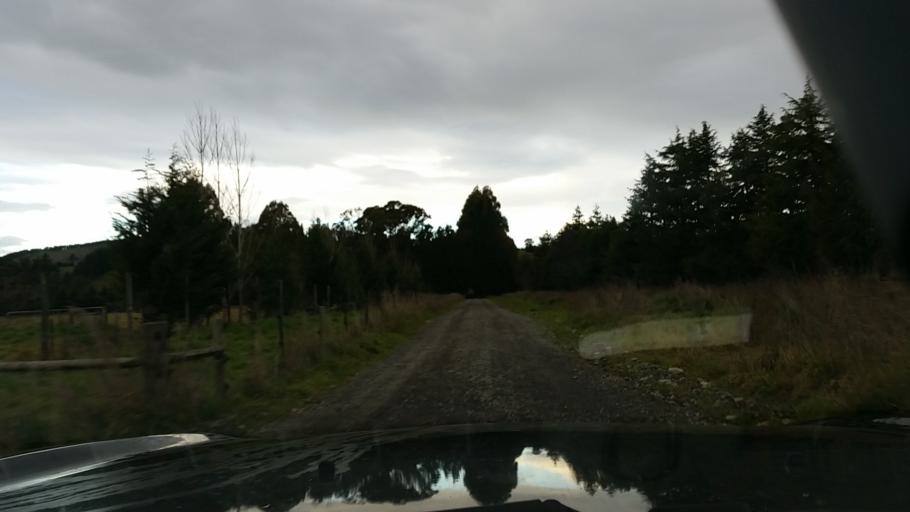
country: NZ
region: Marlborough
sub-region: Marlborough District
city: Blenheim
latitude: -41.5341
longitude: 173.6128
